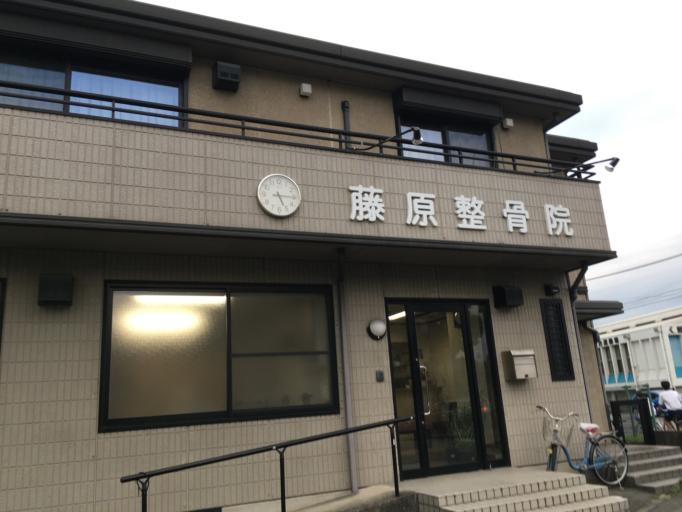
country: JP
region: Kumamoto
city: Kumamoto
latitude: 32.8068
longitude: 130.7289
